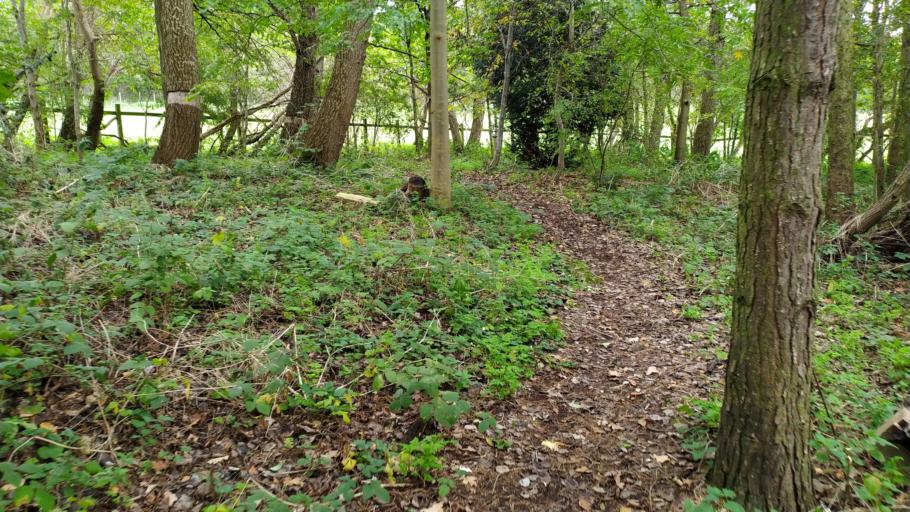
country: GB
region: England
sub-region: City and Borough of Leeds
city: Chapel Allerton
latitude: 53.8201
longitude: -1.5502
